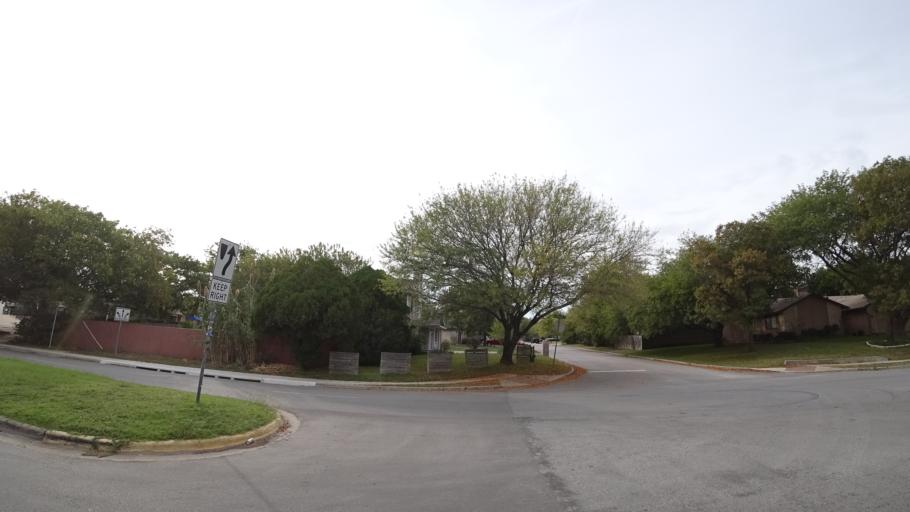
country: US
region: Texas
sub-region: Williamson County
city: Round Rock
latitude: 30.4972
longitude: -97.6653
